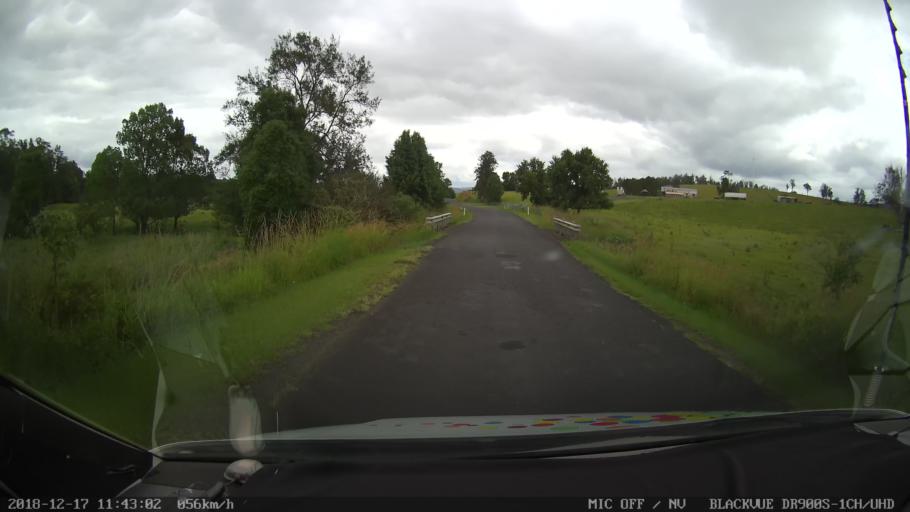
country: AU
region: New South Wales
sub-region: Kyogle
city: Kyogle
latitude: -28.6636
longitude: 152.5927
